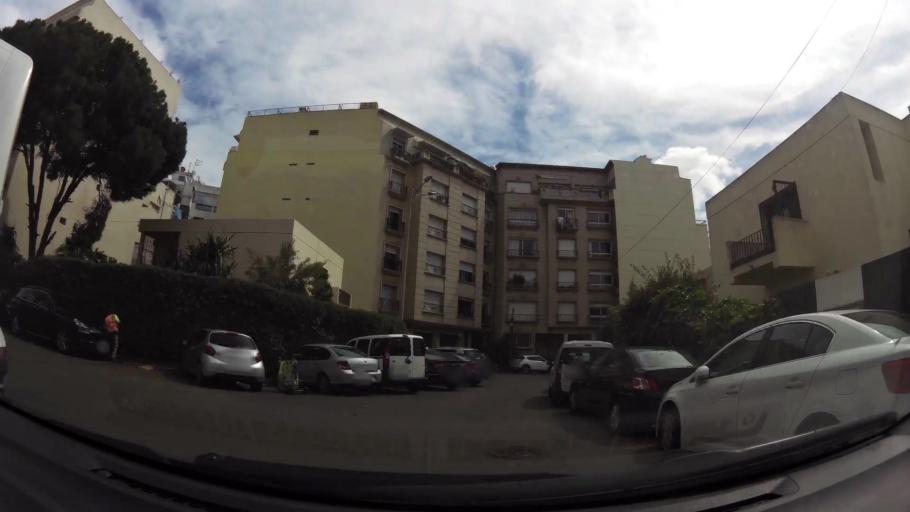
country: MA
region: Grand Casablanca
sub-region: Casablanca
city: Casablanca
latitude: 33.5844
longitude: -7.6448
